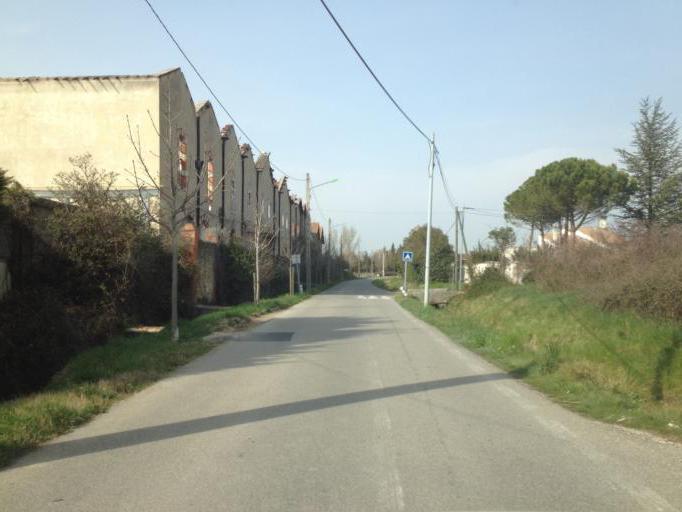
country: FR
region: Provence-Alpes-Cote d'Azur
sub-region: Departement du Vaucluse
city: Bedarrides
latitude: 44.0455
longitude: 4.9003
